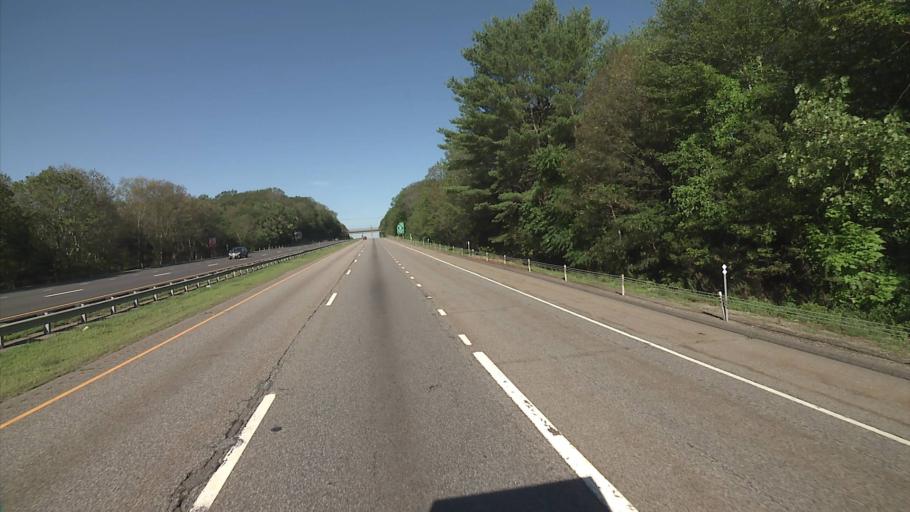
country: US
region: Connecticut
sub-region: New London County
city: Lisbon
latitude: 41.5883
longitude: -72.0258
